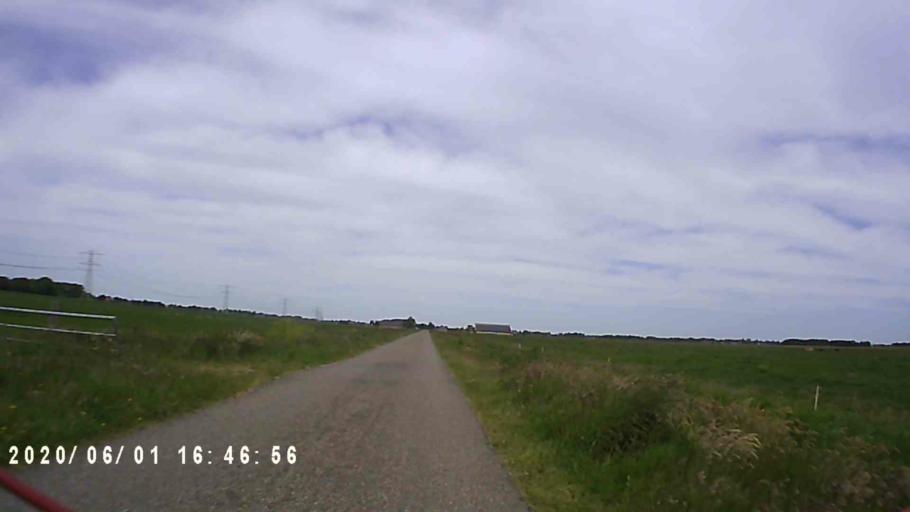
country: NL
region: Friesland
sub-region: Gemeente Tytsjerksteradiel
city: Tytsjerk
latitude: 53.1863
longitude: 5.8938
